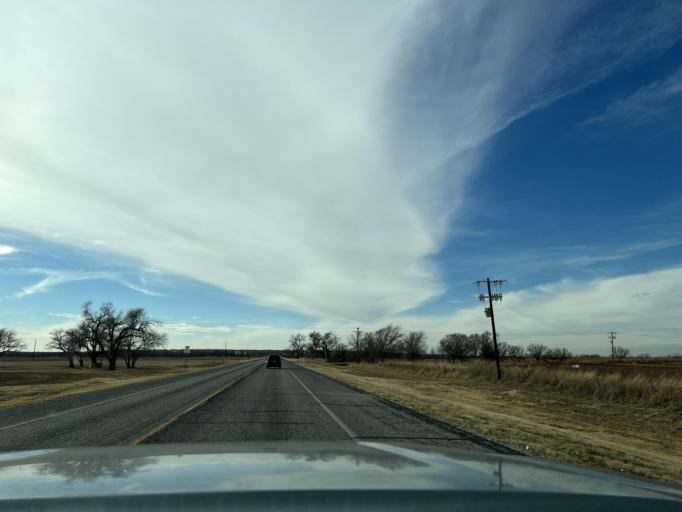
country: US
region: Texas
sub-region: Fisher County
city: Roby
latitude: 32.7612
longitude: -100.3000
